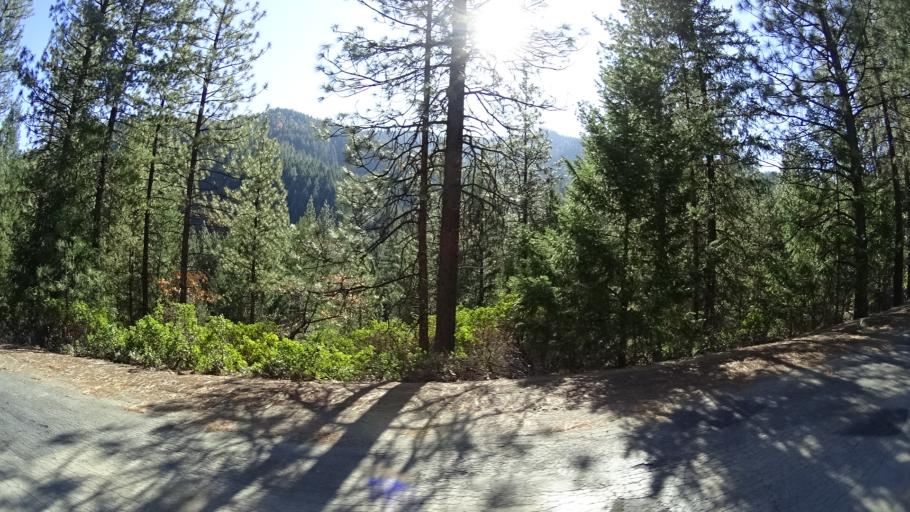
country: US
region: California
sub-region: Siskiyou County
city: Yreka
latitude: 41.7291
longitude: -122.7174
